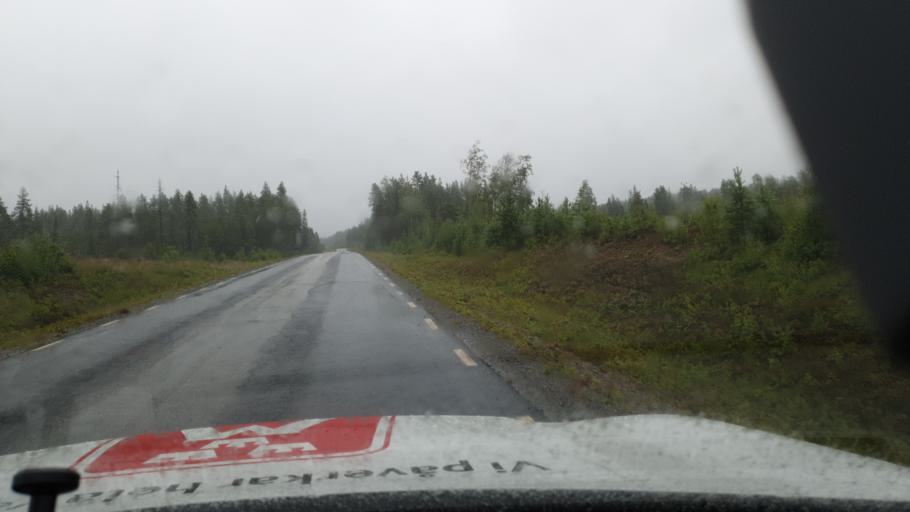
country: SE
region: Vaesterbotten
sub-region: Skelleftea Kommun
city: Langsele
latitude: 64.6505
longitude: 20.0040
